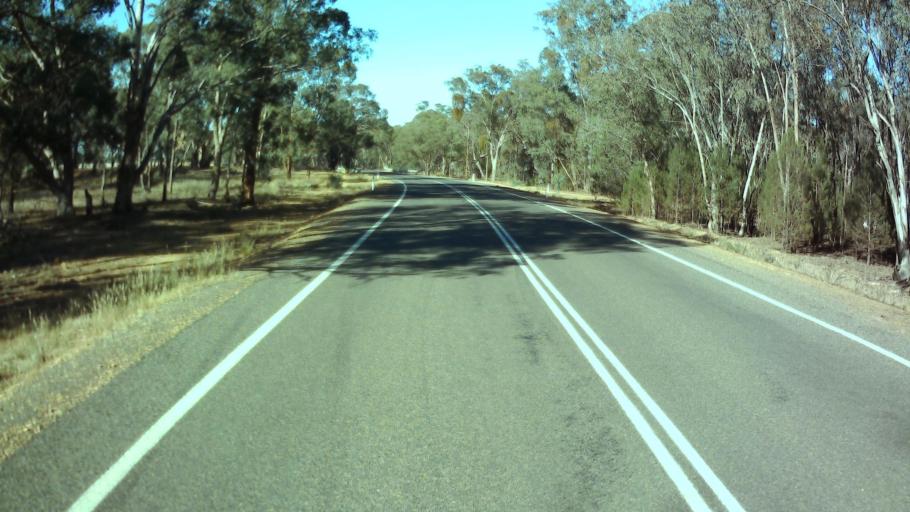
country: AU
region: New South Wales
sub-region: Weddin
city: Grenfell
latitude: -34.0022
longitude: 148.1273
